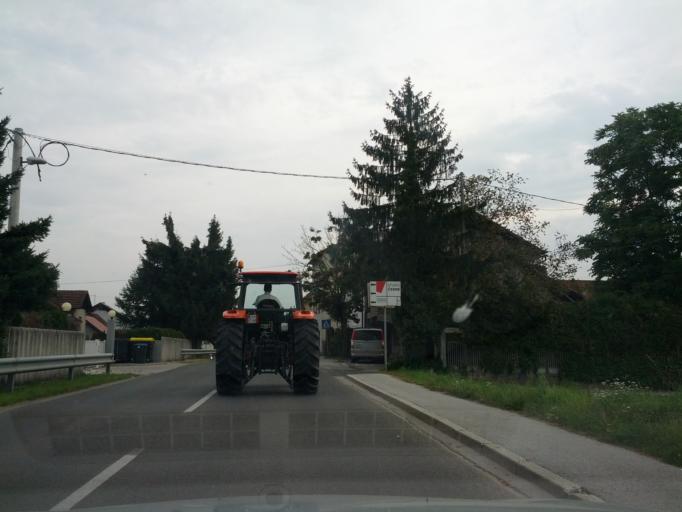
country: SI
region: Dol pri Ljubljani
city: Dol pri Ljubljani
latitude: 46.0756
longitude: 14.5668
